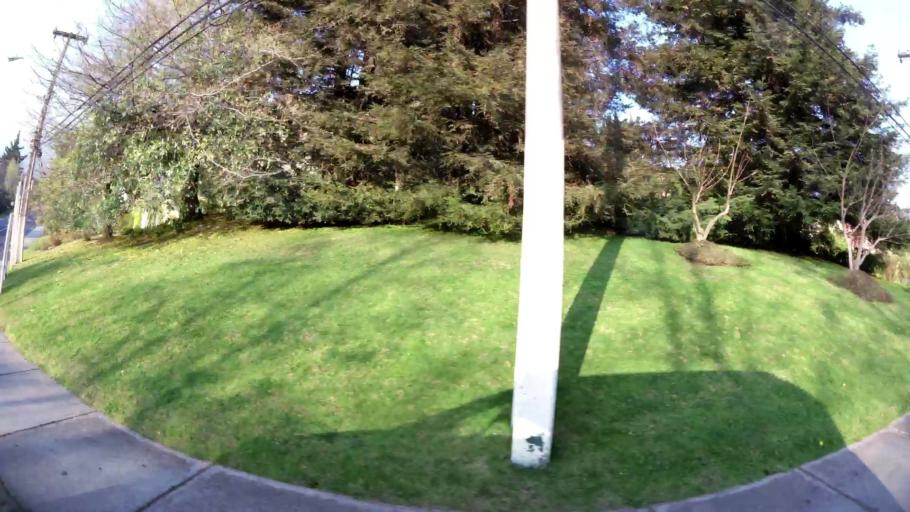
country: CL
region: Santiago Metropolitan
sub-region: Provincia de Santiago
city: Villa Presidente Frei, Nunoa, Santiago, Chile
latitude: -33.3386
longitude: -70.5109
